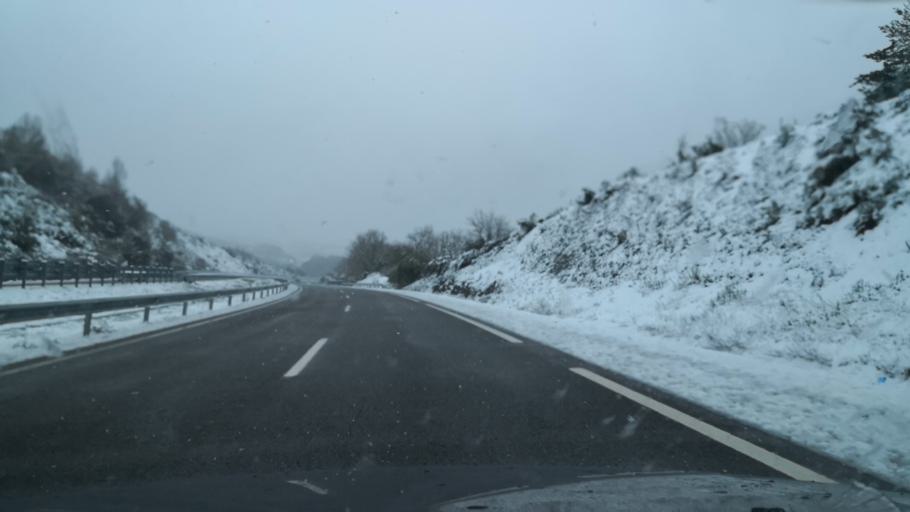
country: ES
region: Galicia
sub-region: Provincia de Ourense
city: Rios
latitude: 41.9888
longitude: -7.2448
